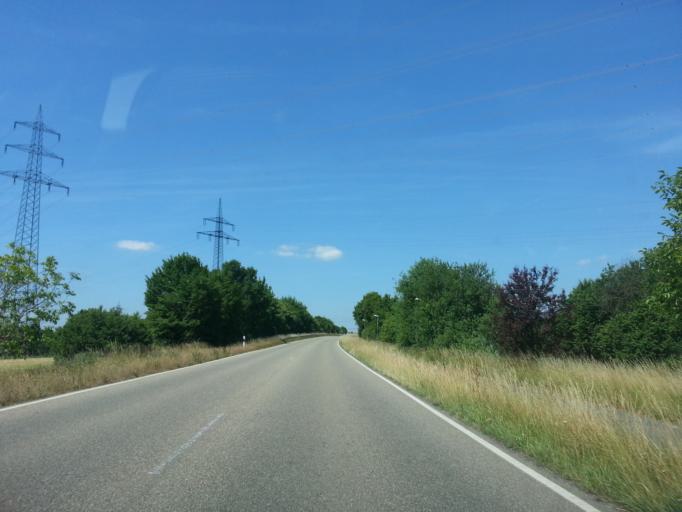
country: DE
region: Baden-Wuerttemberg
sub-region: Karlsruhe Region
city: Bruhl
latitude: 49.3948
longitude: 8.5502
